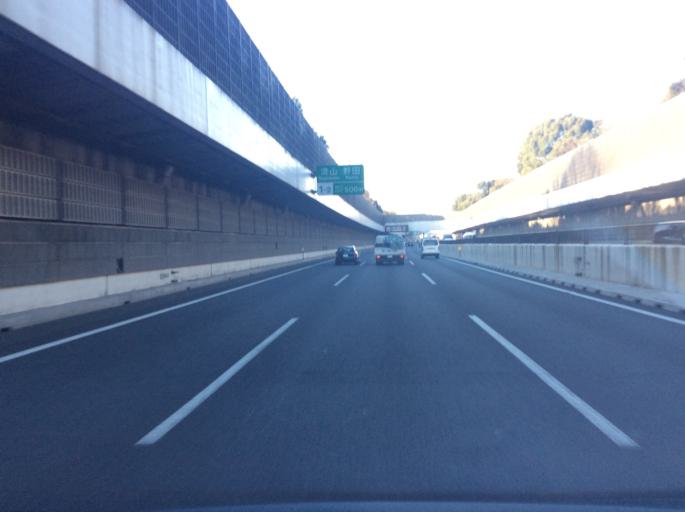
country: JP
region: Chiba
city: Nagareyama
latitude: 35.8828
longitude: 139.9078
